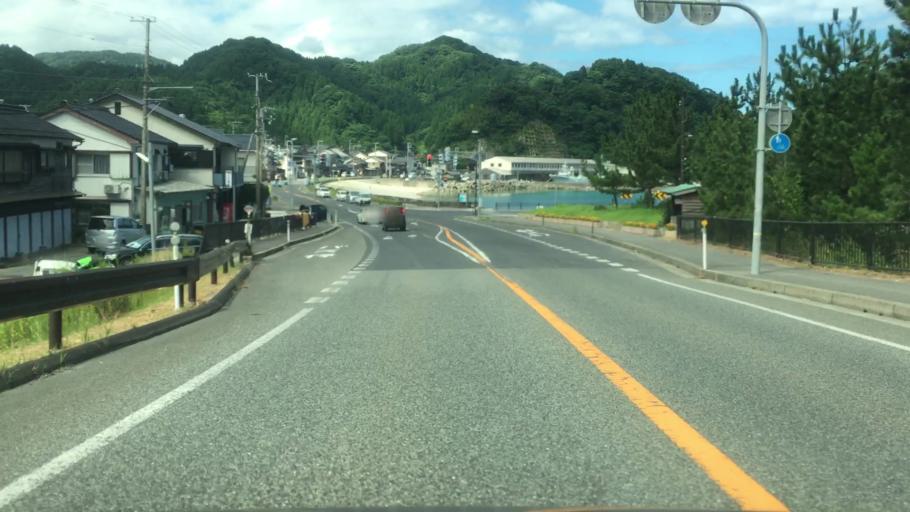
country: JP
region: Tottori
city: Tottori
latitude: 35.6213
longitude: 134.4352
